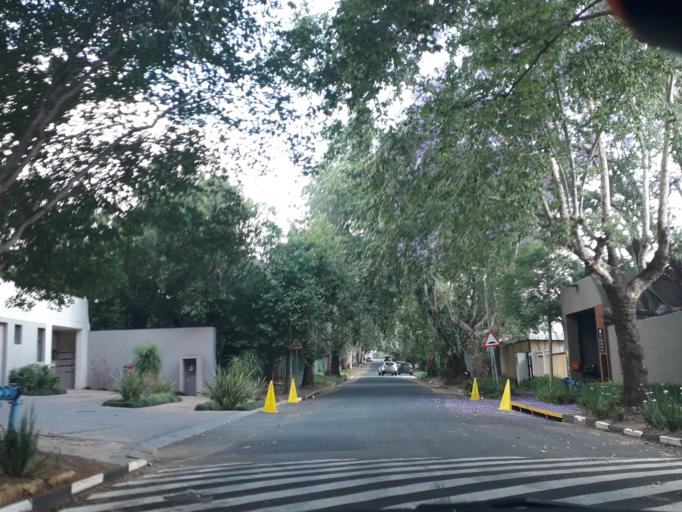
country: ZA
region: Gauteng
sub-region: City of Johannesburg Metropolitan Municipality
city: Johannesburg
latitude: -26.1404
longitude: 28.0376
